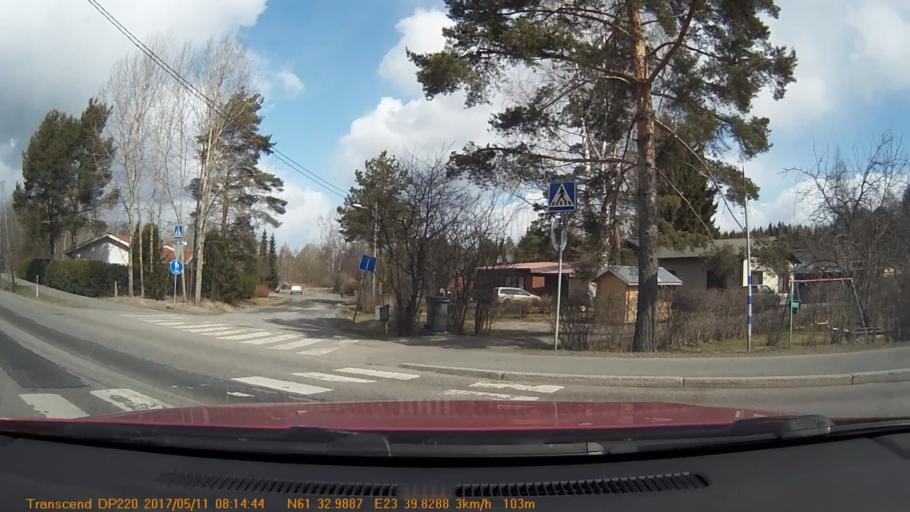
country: FI
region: Pirkanmaa
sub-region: Tampere
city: Yloejaervi
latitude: 61.5498
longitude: 23.6638
